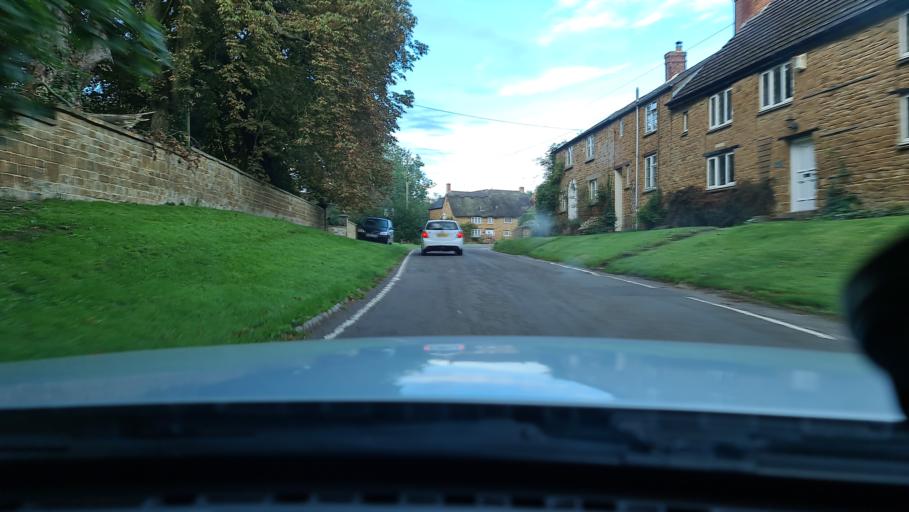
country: GB
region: England
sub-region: Oxfordshire
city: Hanwell
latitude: 52.0907
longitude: -1.3660
